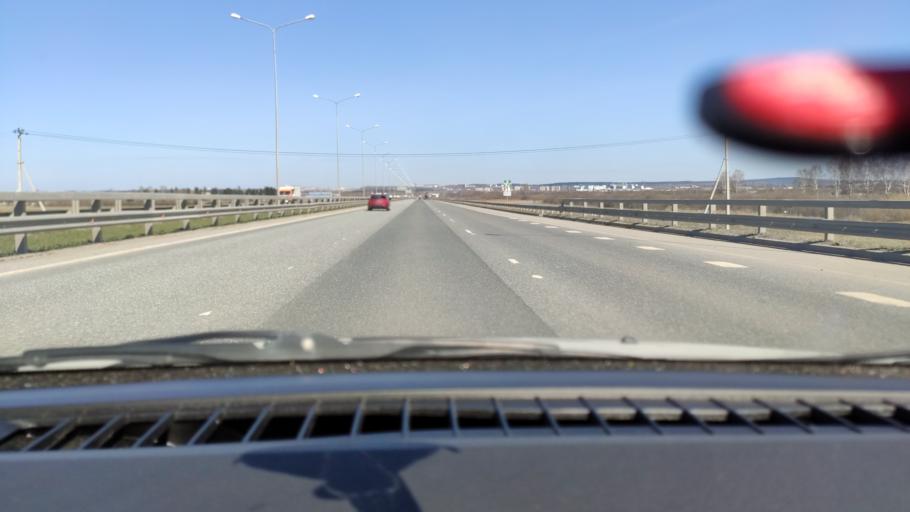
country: RU
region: Perm
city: Froly
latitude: 57.8852
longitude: 56.2658
